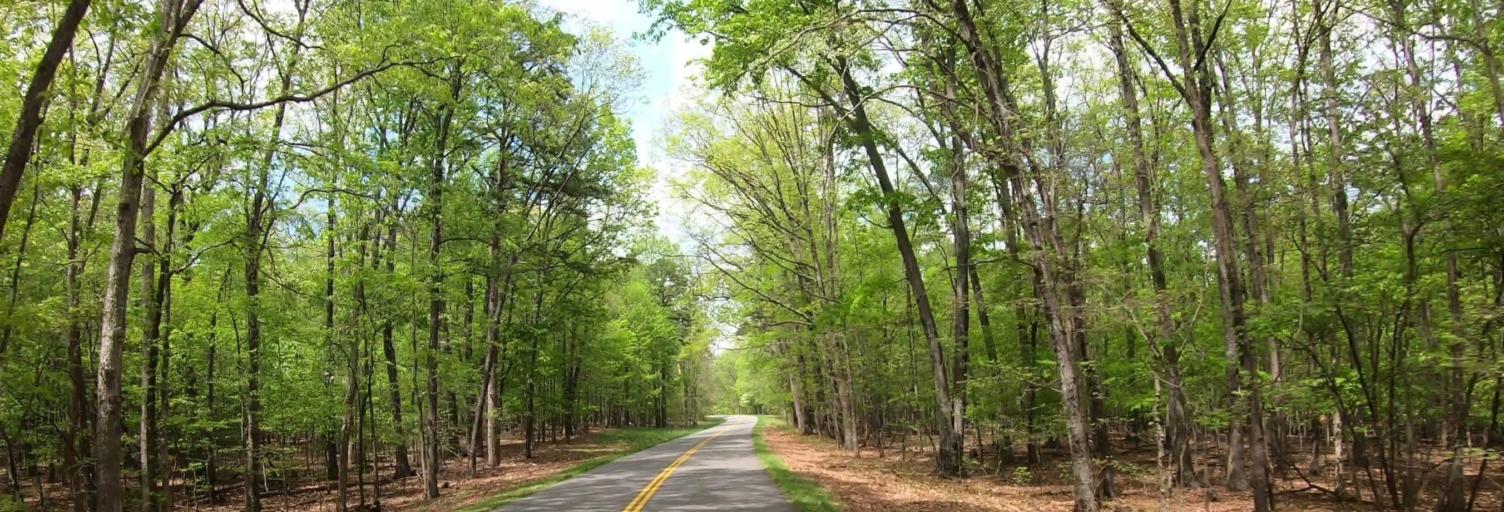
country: US
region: Virginia
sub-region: Botetourt County
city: Laymantown
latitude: 37.3797
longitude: -79.8392
